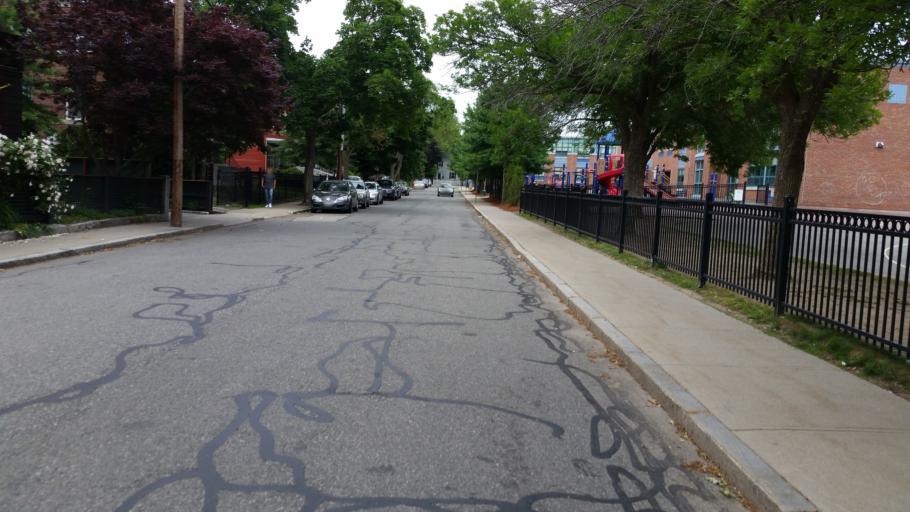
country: US
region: Massachusetts
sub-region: Middlesex County
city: Cambridge
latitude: 42.3913
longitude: -71.1291
